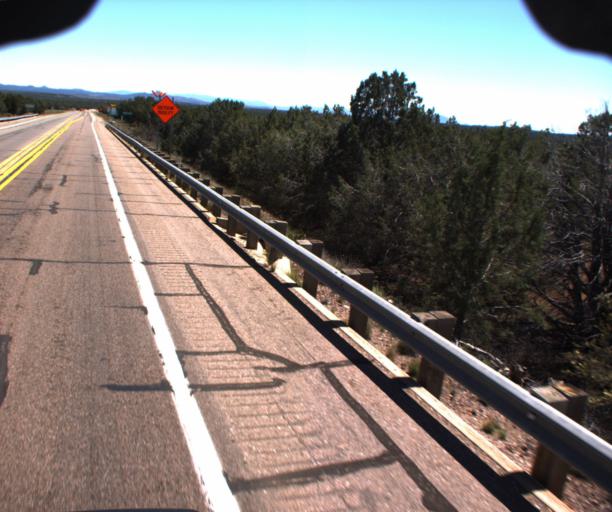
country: US
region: Arizona
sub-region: Yavapai County
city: Paulden
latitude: 35.0083
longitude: -112.3905
